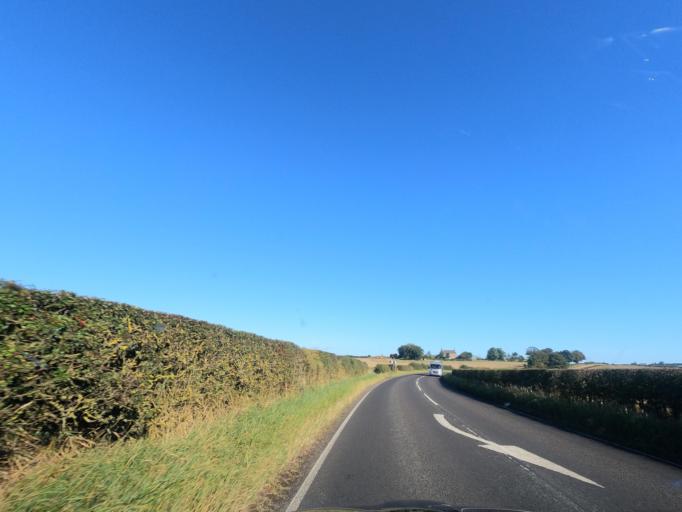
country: GB
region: England
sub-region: Northumberland
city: Ford
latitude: 55.7266
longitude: -2.0967
